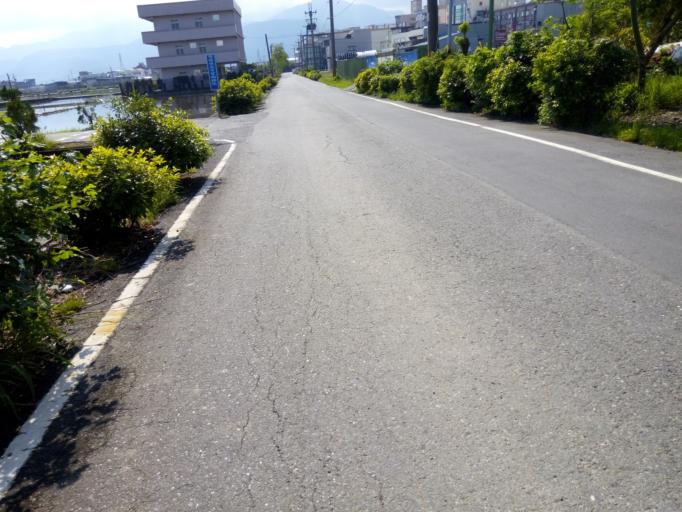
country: TW
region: Taiwan
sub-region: Yilan
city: Yilan
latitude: 24.6717
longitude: 121.7789
